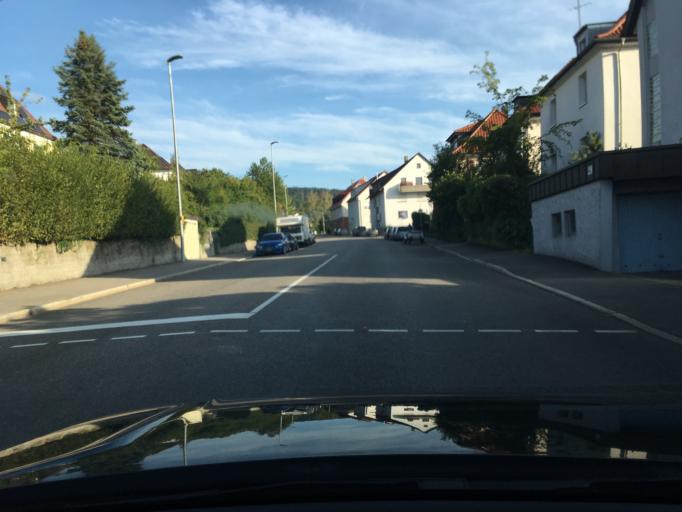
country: DE
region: Baden-Wuerttemberg
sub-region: Regierungsbezirk Stuttgart
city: Schorndorf
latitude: 48.8028
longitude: 9.5359
